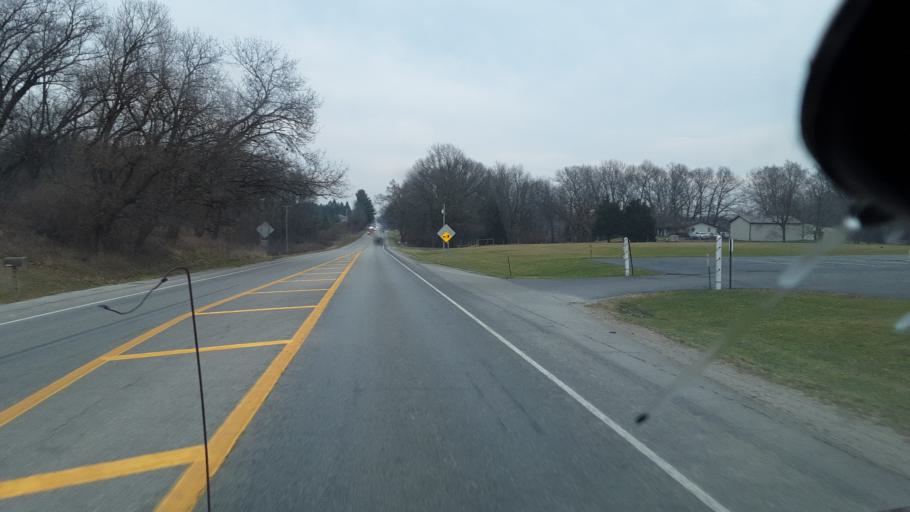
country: US
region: Indiana
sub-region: Elkhart County
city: Middlebury
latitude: 41.7257
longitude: -85.6818
